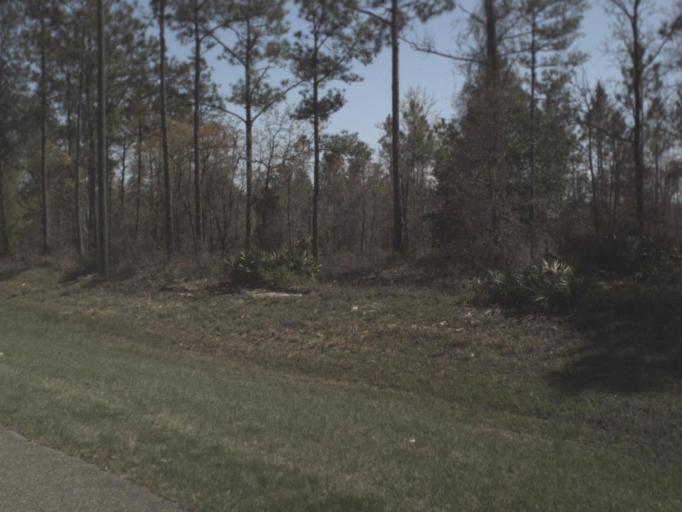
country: US
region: Florida
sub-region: Liberty County
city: Bristol
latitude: 30.4121
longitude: -84.8535
